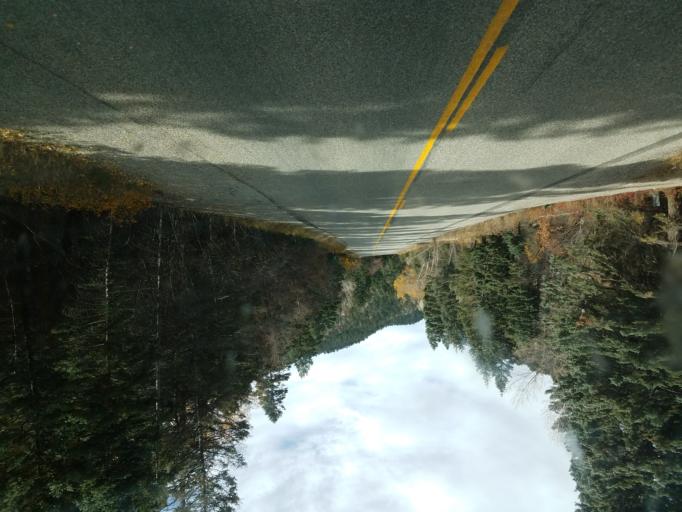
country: US
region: New Mexico
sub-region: Taos County
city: Arroyo Seco
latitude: 36.5498
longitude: -105.5463
